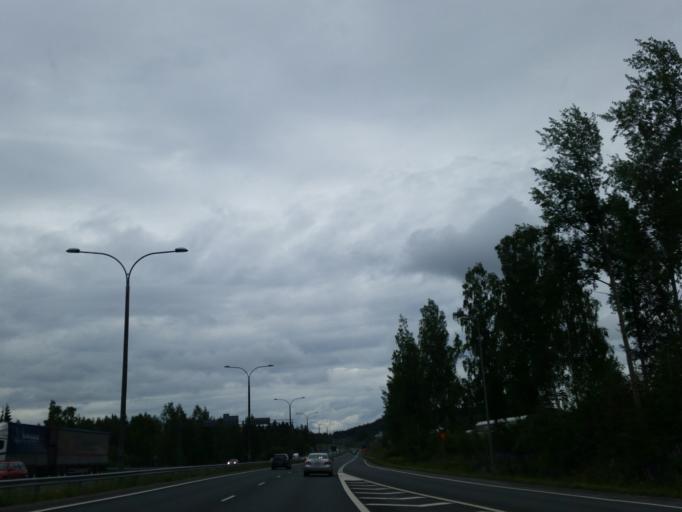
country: FI
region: Northern Savo
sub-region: Kuopio
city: Kuopio
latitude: 62.9604
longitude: 27.6922
